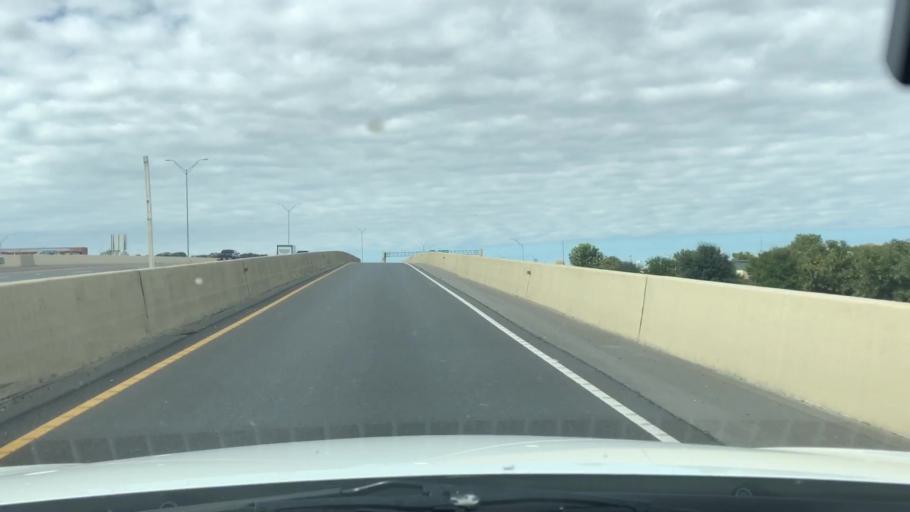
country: US
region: Texas
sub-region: Bexar County
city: Lackland Air Force Base
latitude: 29.4382
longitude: -98.6566
